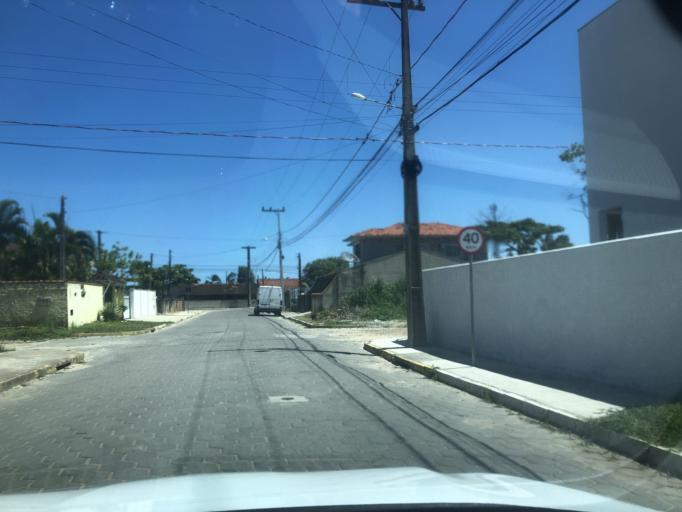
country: BR
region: Santa Catarina
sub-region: Sao Francisco Do Sul
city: Sao Francisco do Sul
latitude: -26.2237
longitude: -48.5249
